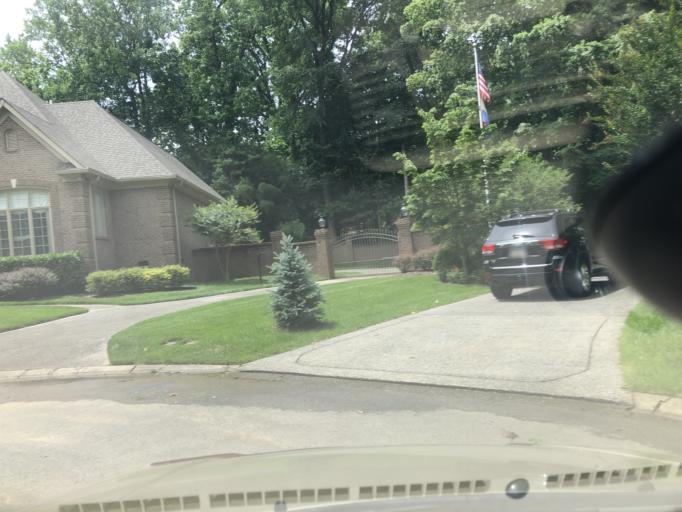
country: US
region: Tennessee
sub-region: Davidson County
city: Lakewood
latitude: 36.2589
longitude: -86.5870
